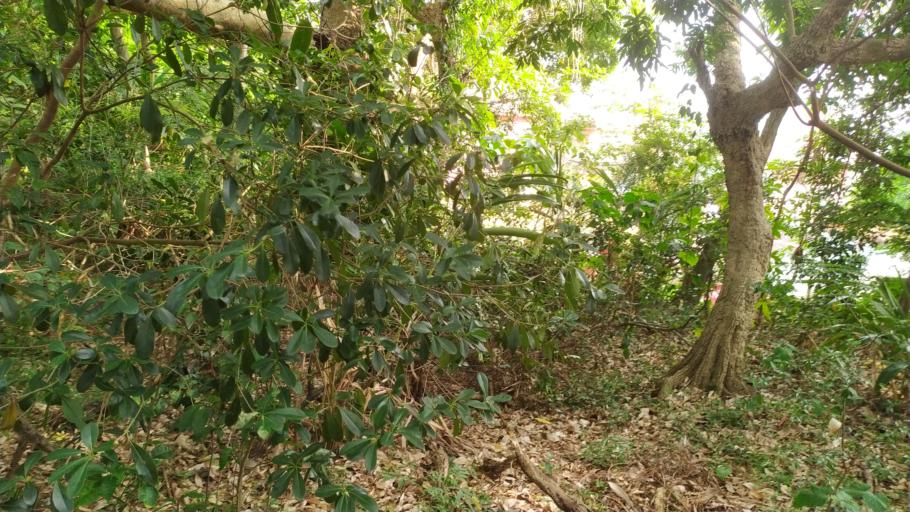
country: TW
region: Taipei
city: Taipei
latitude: 25.1036
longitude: 121.5307
